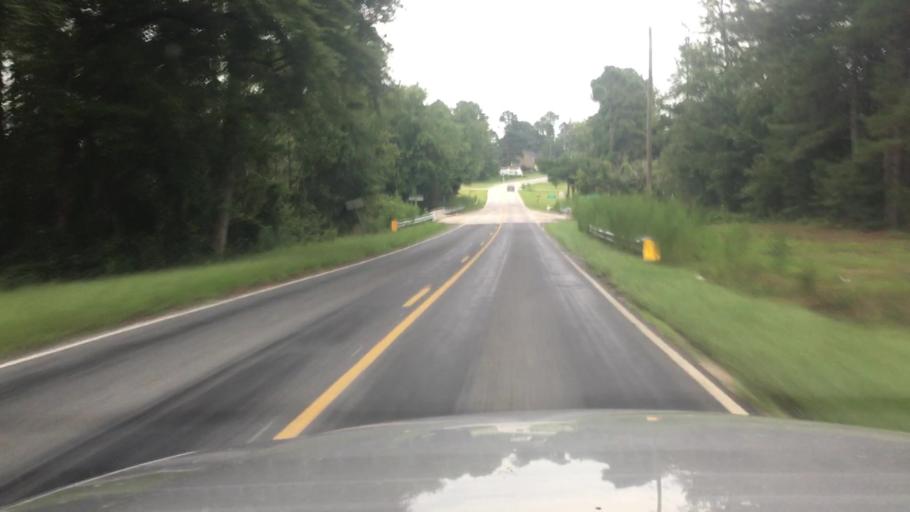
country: US
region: North Carolina
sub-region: Hoke County
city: Rockfish
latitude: 34.9811
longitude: -79.0490
